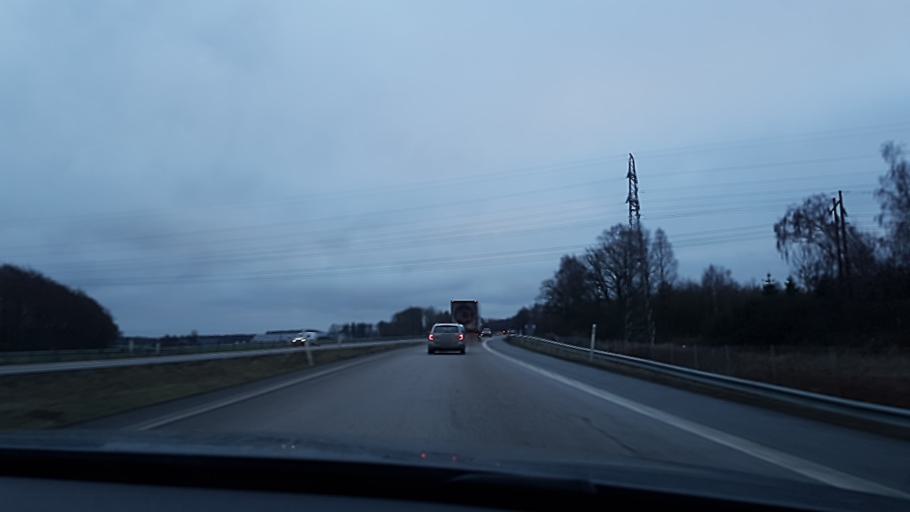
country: SE
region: Skane
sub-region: Helsingborg
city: Odakra
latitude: 56.0817
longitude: 12.7781
